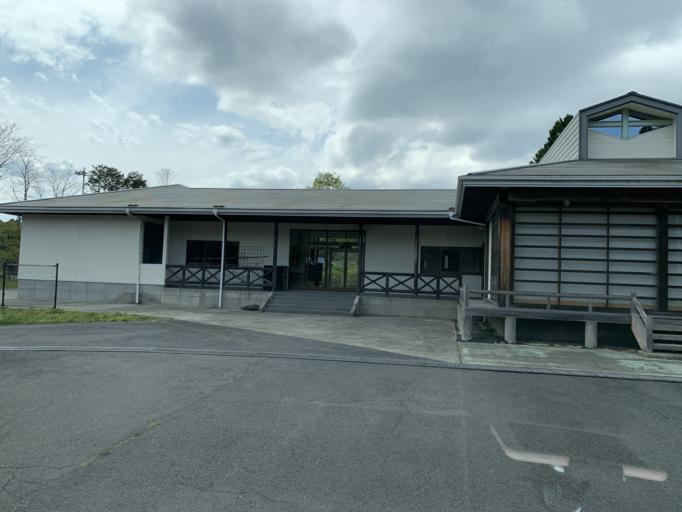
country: JP
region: Iwate
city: Ichinoseki
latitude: 38.7930
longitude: 141.4052
